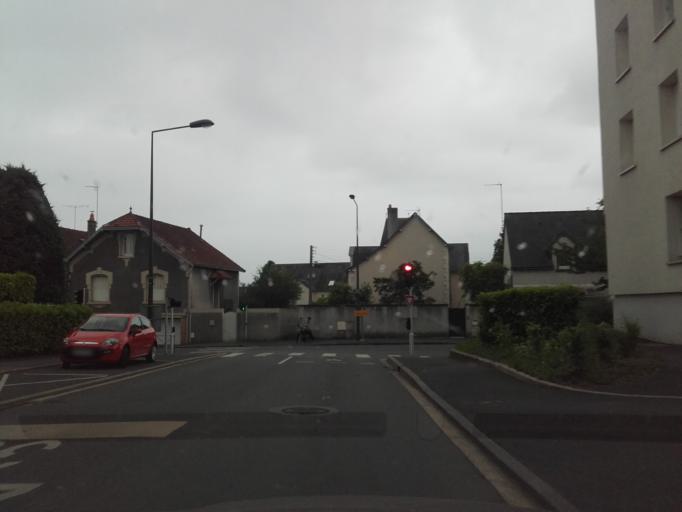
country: FR
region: Centre
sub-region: Departement d'Indre-et-Loire
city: Saint-Cyr-sur-Loire
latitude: 47.4119
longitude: 0.6875
